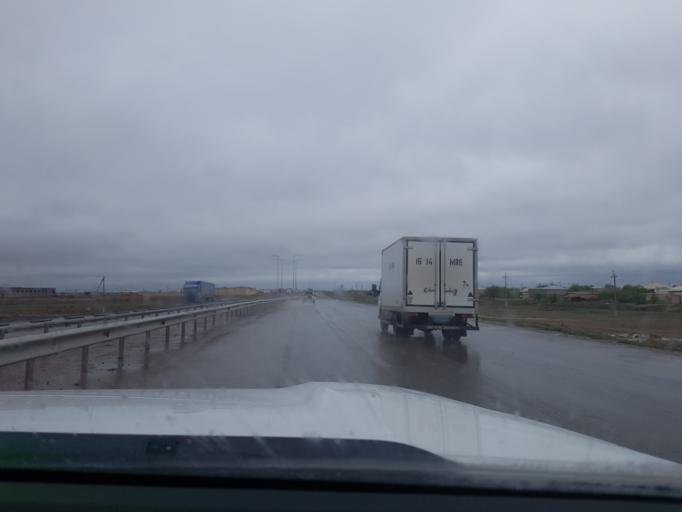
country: TM
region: Mary
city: Bayramaly
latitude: 37.6129
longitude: 62.1174
